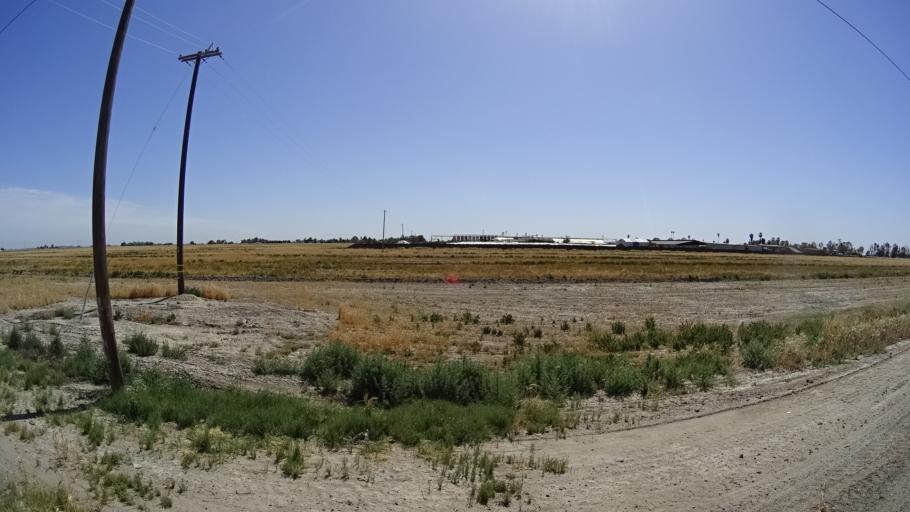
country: US
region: California
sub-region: Kings County
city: Stratford
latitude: 36.1930
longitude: -119.8340
